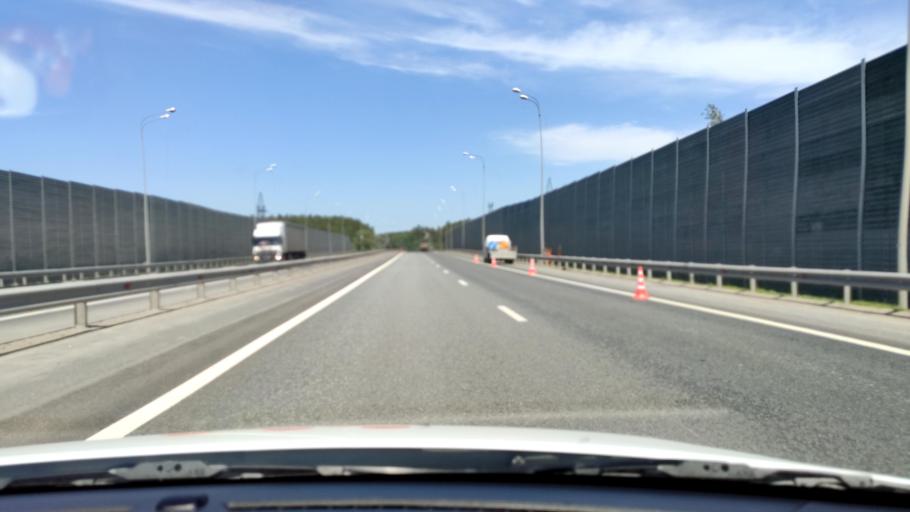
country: RU
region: Tatarstan
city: Osinovo
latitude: 55.8217
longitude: 48.8461
